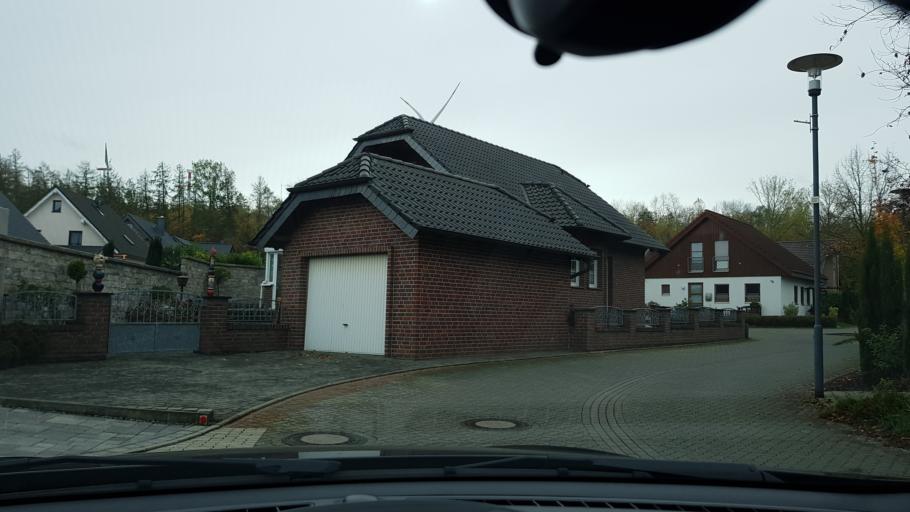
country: DE
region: North Rhine-Westphalia
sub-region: Regierungsbezirk Dusseldorf
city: Grevenbroich
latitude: 51.0418
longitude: 6.5770
